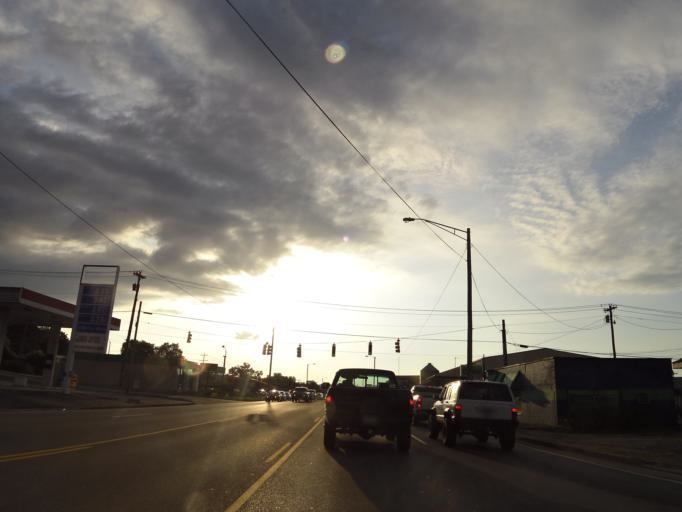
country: US
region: Tennessee
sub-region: Cocke County
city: Newport
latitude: 35.9695
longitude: -83.2051
